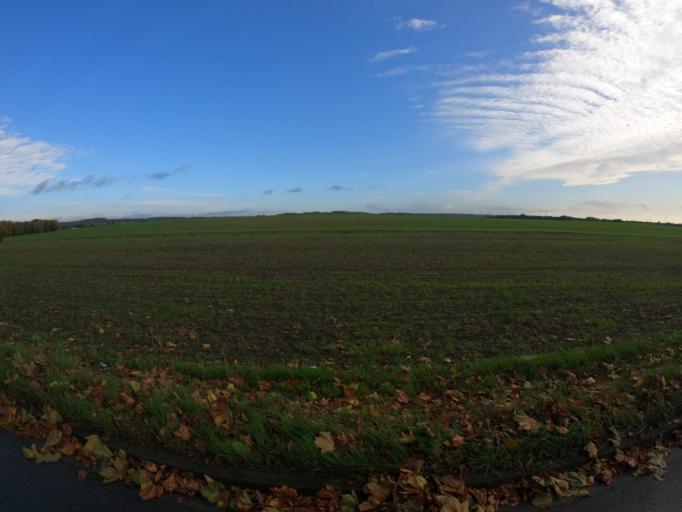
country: FR
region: Ile-de-France
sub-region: Departement de Seine-et-Marne
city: Le Pin
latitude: 48.8981
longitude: 2.6191
